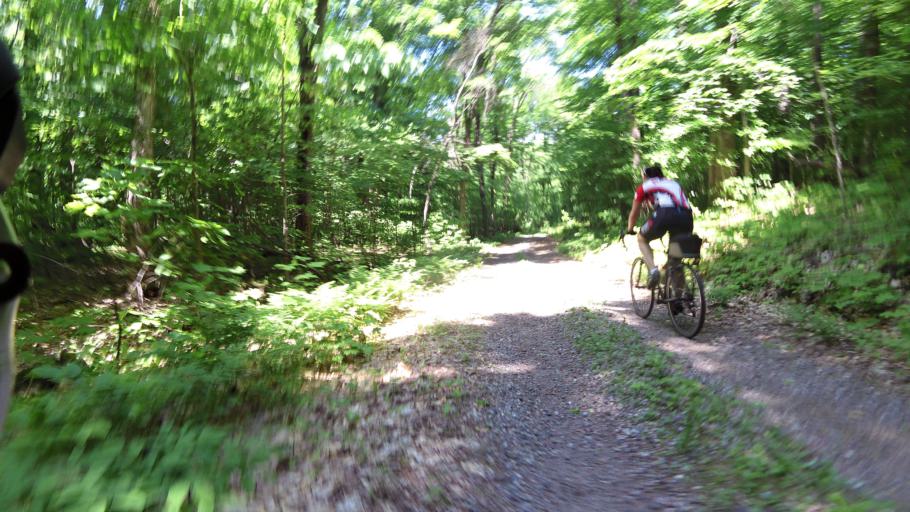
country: CA
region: Quebec
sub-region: Outaouais
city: Wakefield
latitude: 45.5757
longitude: -75.9446
